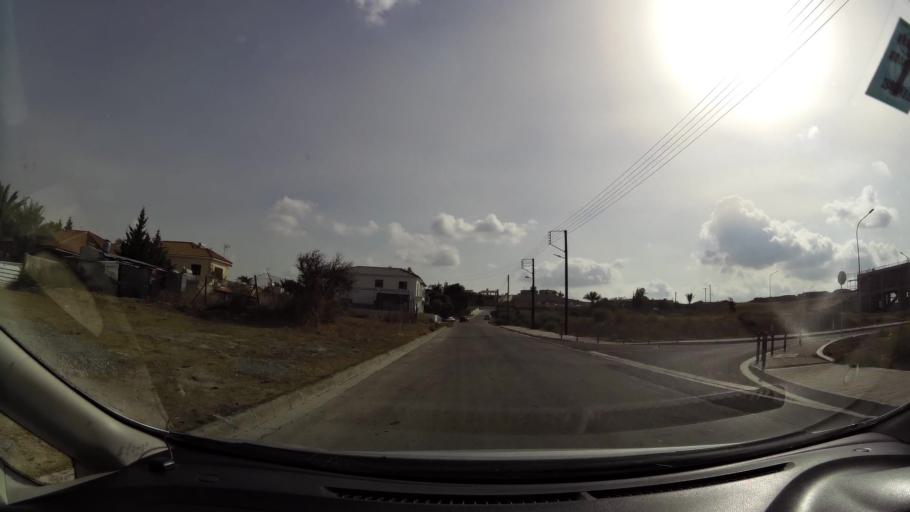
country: CY
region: Lefkosia
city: Dali
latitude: 35.0608
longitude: 33.3982
